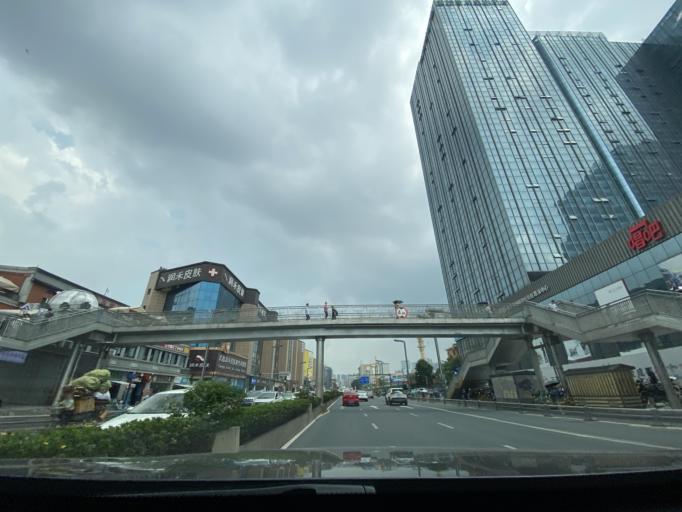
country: CN
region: Sichuan
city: Chengdu
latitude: 30.6321
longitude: 104.0739
